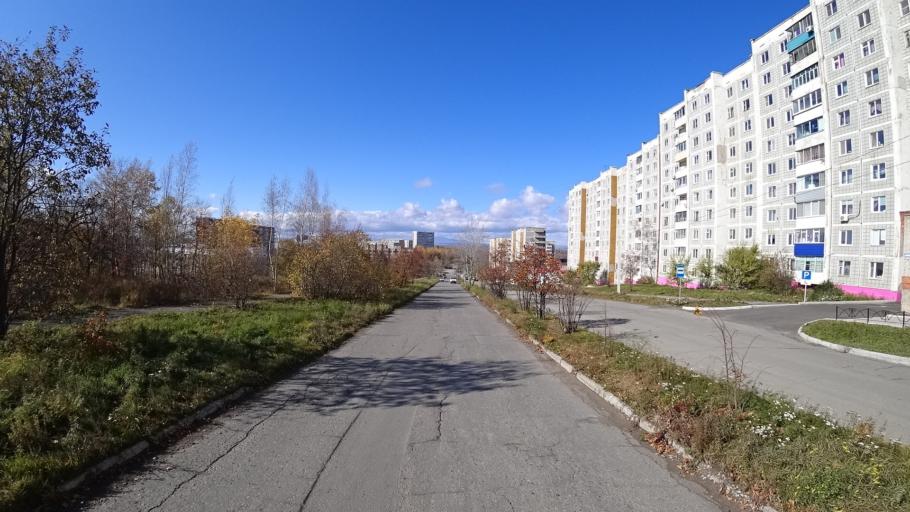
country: RU
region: Khabarovsk Krai
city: Amursk
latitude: 50.2426
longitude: 136.9197
